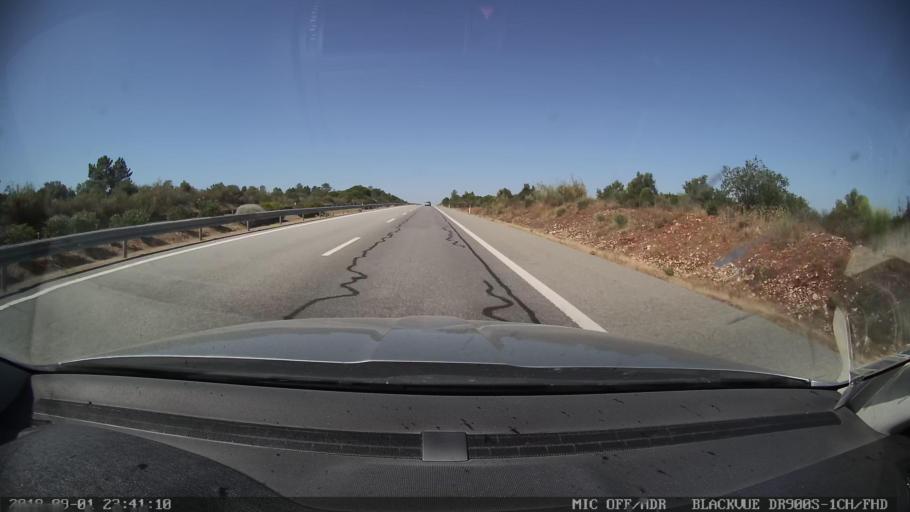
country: PT
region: Evora
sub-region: Borba
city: Borba
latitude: 38.8110
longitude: -7.5142
